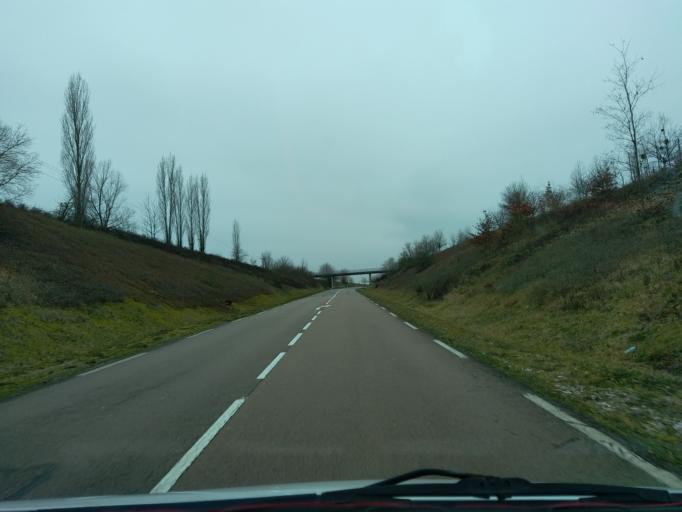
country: FR
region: Franche-Comte
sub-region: Departement de la Haute-Saone
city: Gray-la-Ville
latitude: 47.4179
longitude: 5.5191
